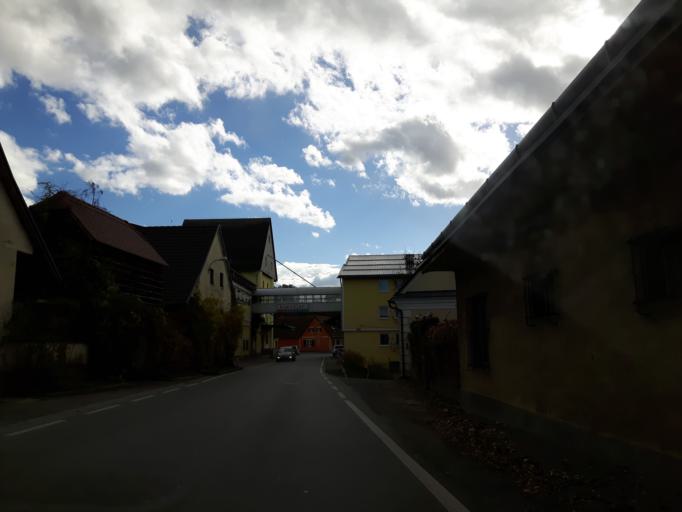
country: AT
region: Styria
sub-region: Politischer Bezirk Leibnitz
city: Ragnitz
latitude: 46.8340
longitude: 15.5933
